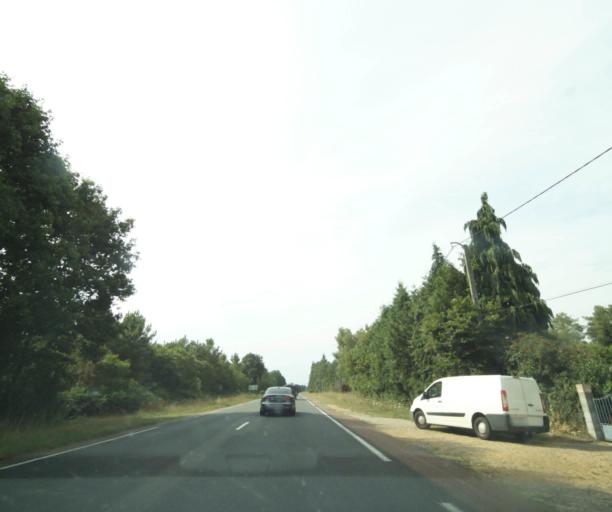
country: FR
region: Pays de la Loire
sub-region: Departement de la Sarthe
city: Marigne-Laille
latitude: 47.7778
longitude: 0.3433
